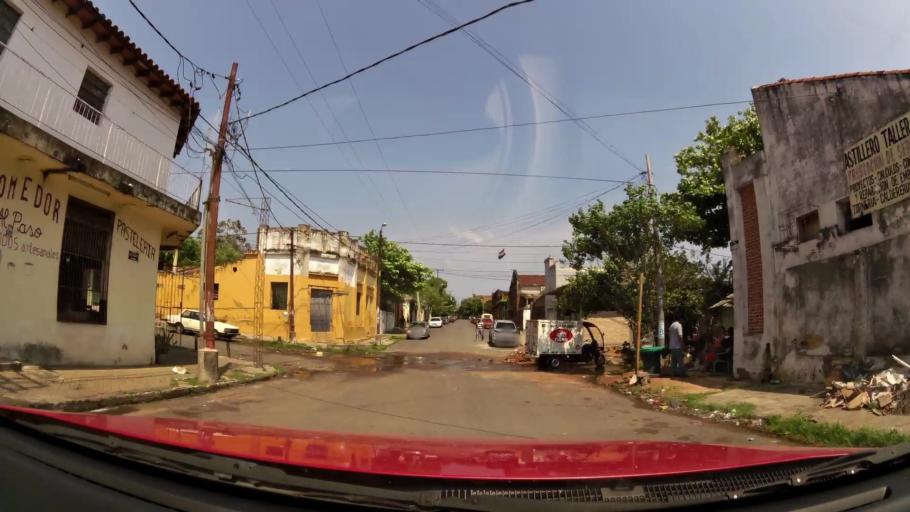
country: PY
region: Presidente Hayes
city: Nanawa
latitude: -25.2770
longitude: -57.6535
